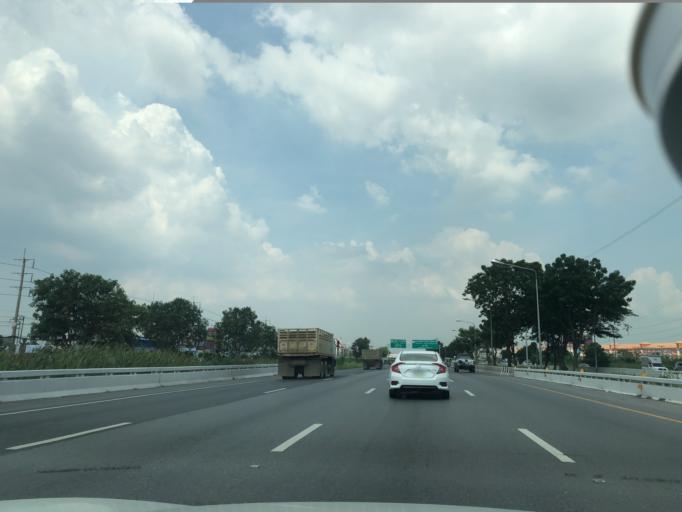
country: TH
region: Phra Nakhon Si Ayutthaya
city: Phra Nakhon Si Ayutthaya
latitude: 14.3263
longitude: 100.6130
